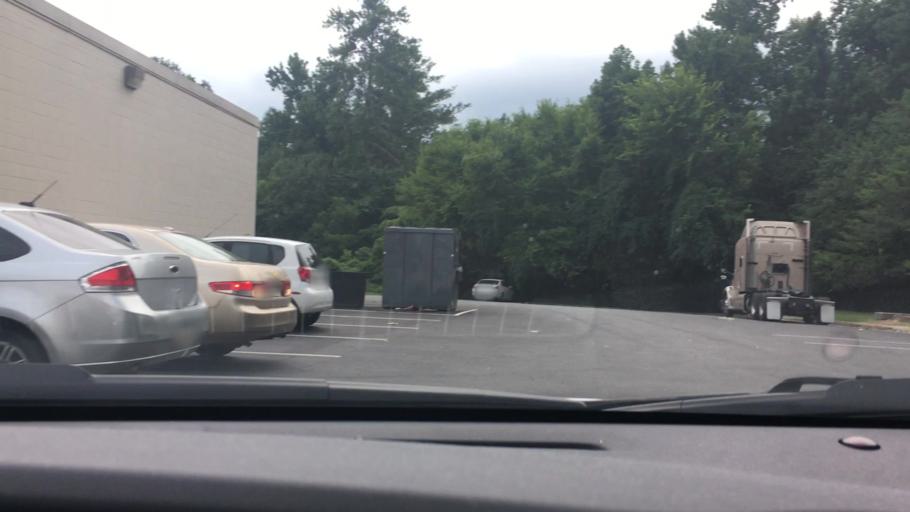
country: US
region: Georgia
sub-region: Cobb County
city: Kennesaw
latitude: 34.0046
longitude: -84.5732
